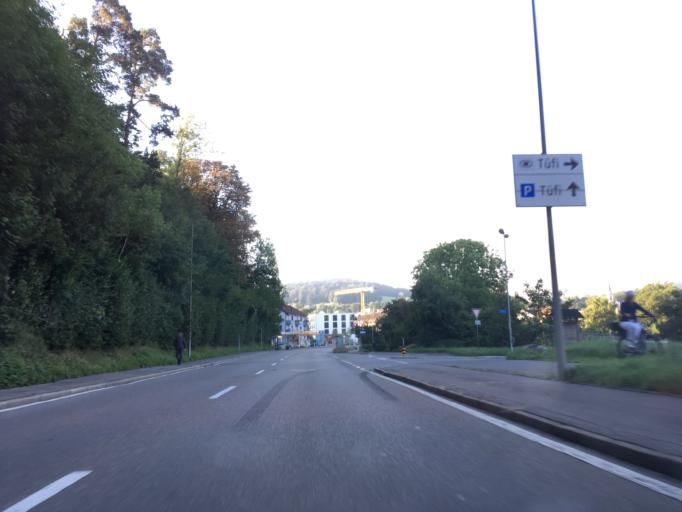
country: CH
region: Zurich
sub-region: Bezirk Horgen
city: Adliswil / Sood
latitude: 47.3175
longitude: 8.5295
